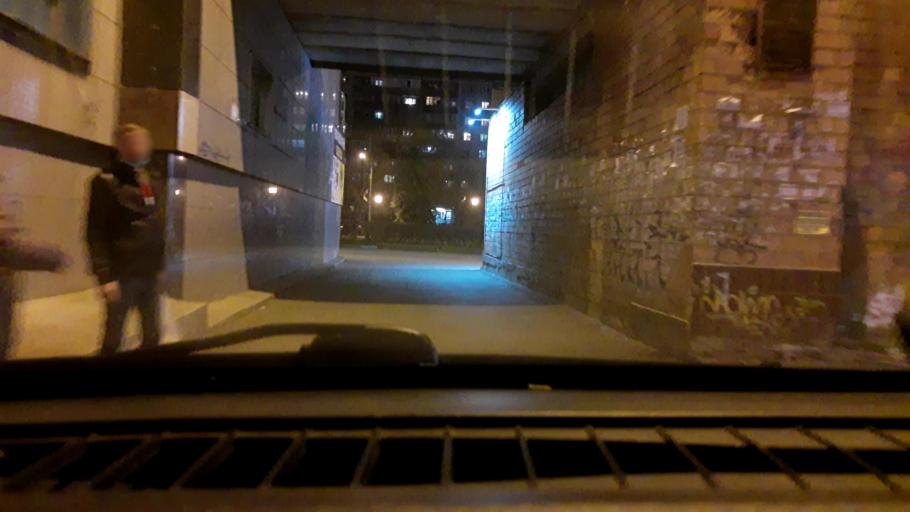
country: RU
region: Nizjnij Novgorod
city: Gorbatovka
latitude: 56.3596
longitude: 43.8212
